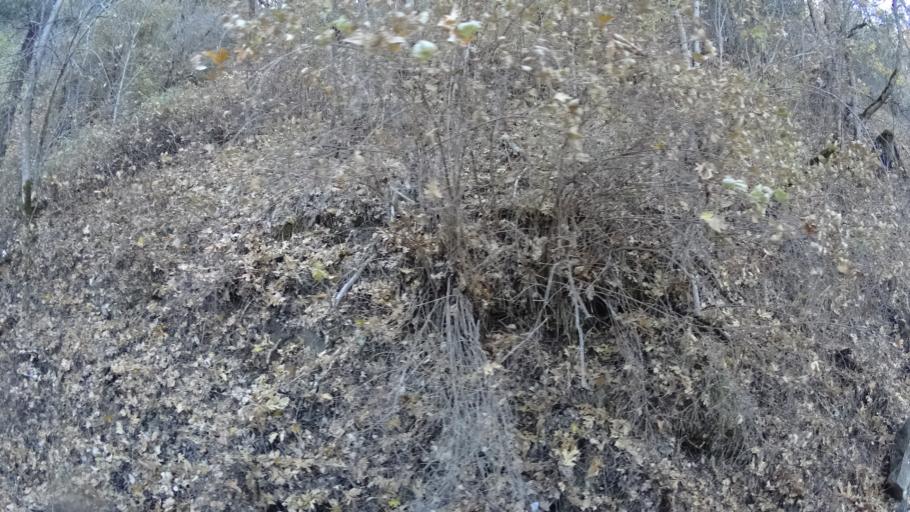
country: US
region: California
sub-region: Siskiyou County
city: Yreka
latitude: 41.8621
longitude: -122.7352
